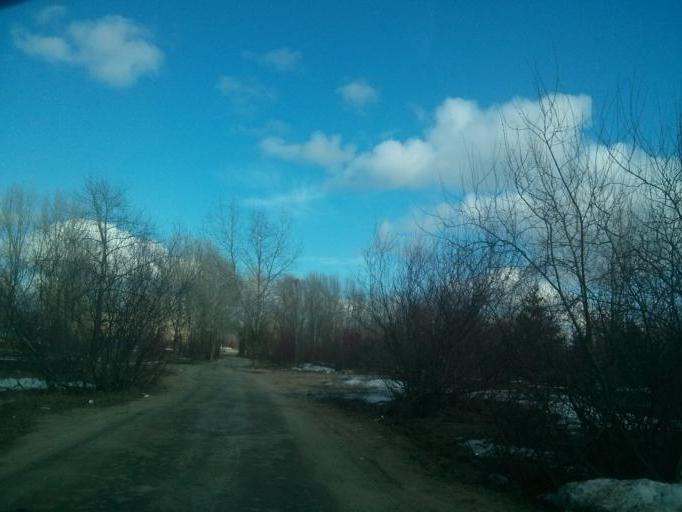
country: RU
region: Nizjnij Novgorod
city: Bor
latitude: 56.3290
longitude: 44.0504
